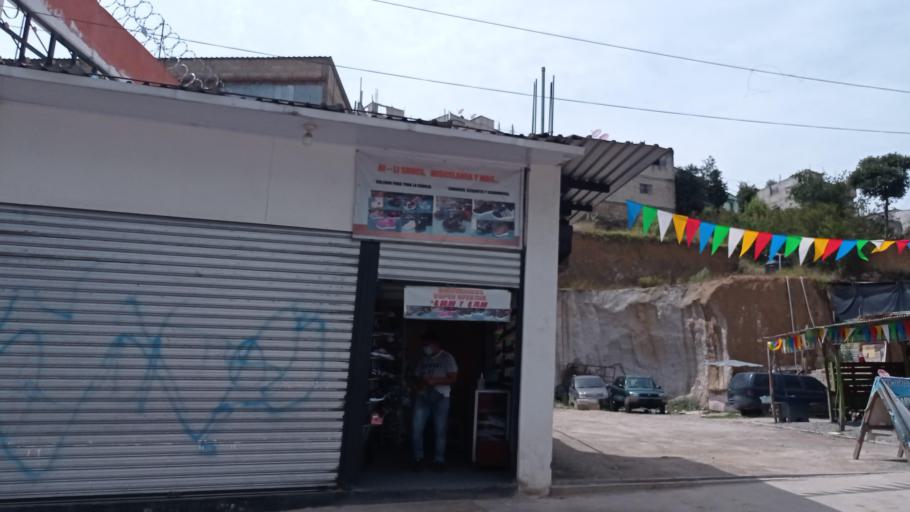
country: GT
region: Quetzaltenango
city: Quetzaltenango
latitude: 14.8463
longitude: -91.5016
